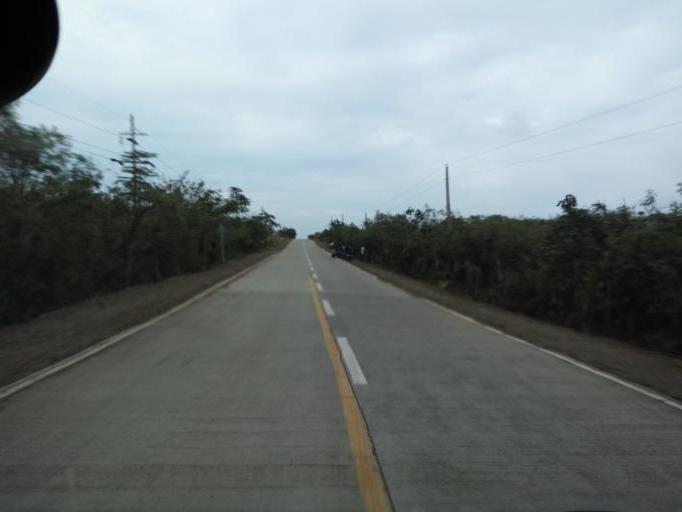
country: PH
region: Cagayan Valley
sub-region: Province of Cagayan
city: Magapit
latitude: 18.1525
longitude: 121.7409
